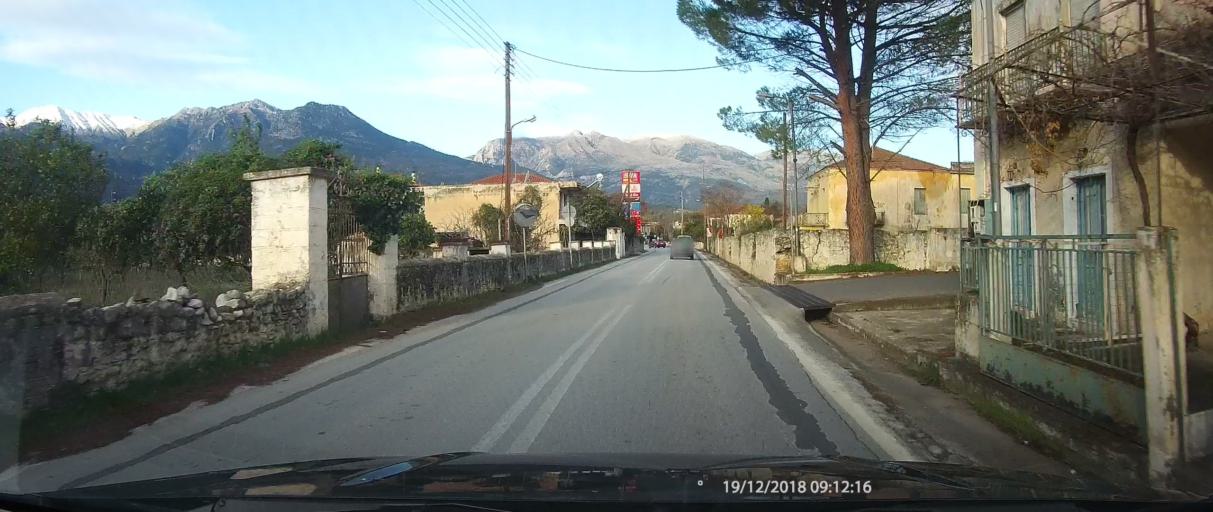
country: GR
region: Peloponnese
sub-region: Nomos Lakonias
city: Magoula
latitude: 37.0790
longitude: 22.4069
